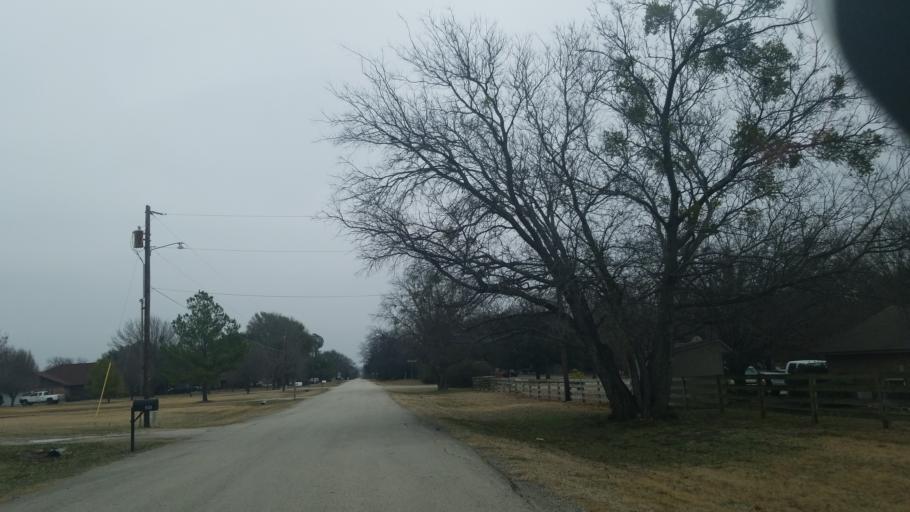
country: US
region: Texas
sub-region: Denton County
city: Argyle
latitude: 33.1472
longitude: -97.1644
